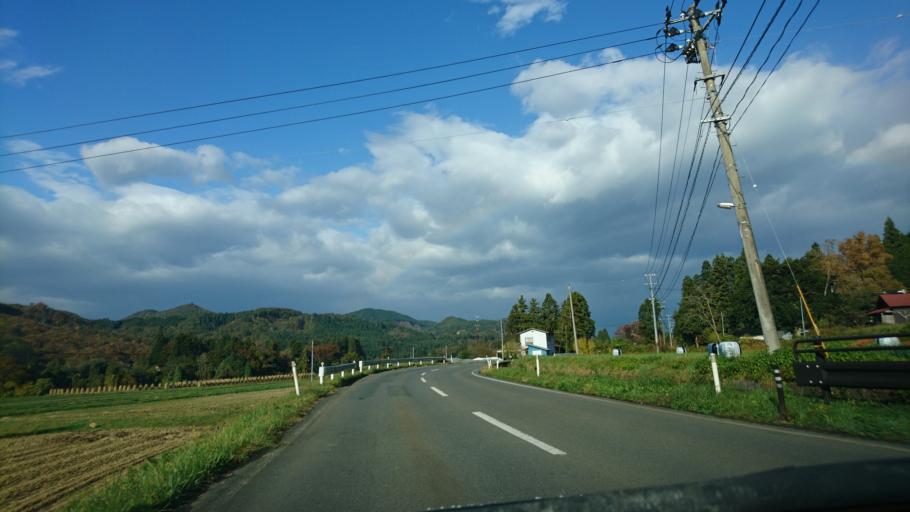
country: JP
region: Iwate
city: Mizusawa
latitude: 39.0477
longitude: 141.0516
